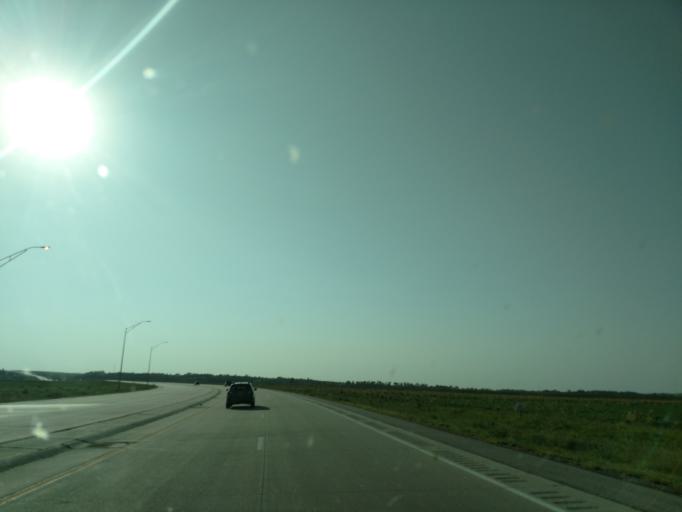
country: US
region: Nebraska
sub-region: Sarpy County
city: Offutt Air Force Base
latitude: 41.0770
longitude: -95.8915
